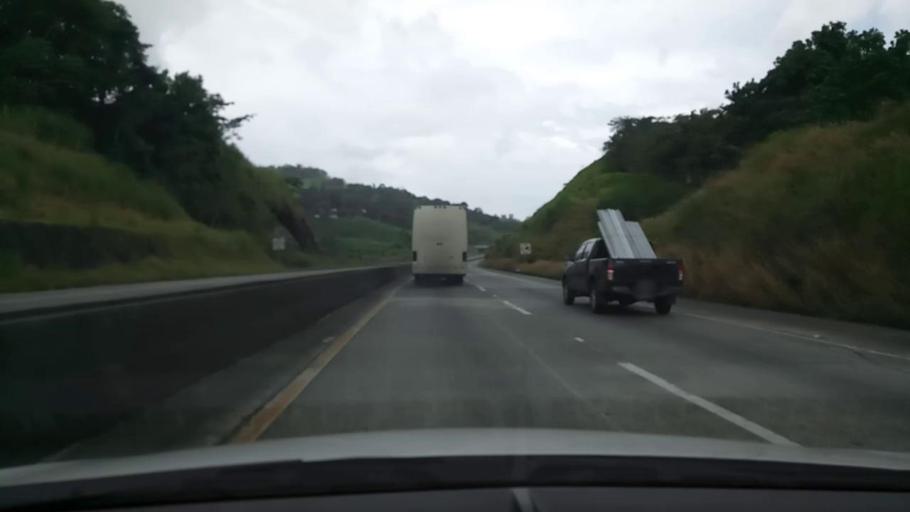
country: PA
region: Colon
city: Gatun
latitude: 9.2826
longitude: -79.7500
